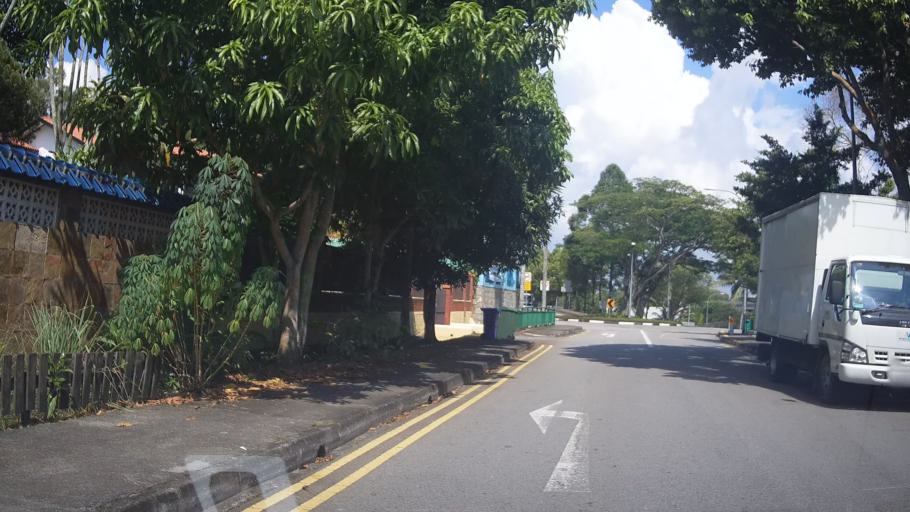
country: MY
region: Johor
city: Kampung Pasir Gudang Baru
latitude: 1.3836
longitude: 103.9441
